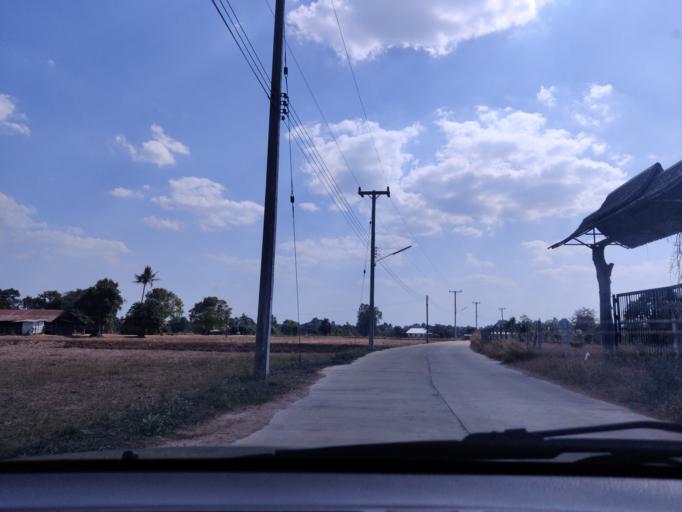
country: TH
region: Sisaket
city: Si Sa Ket
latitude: 15.0855
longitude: 104.3532
